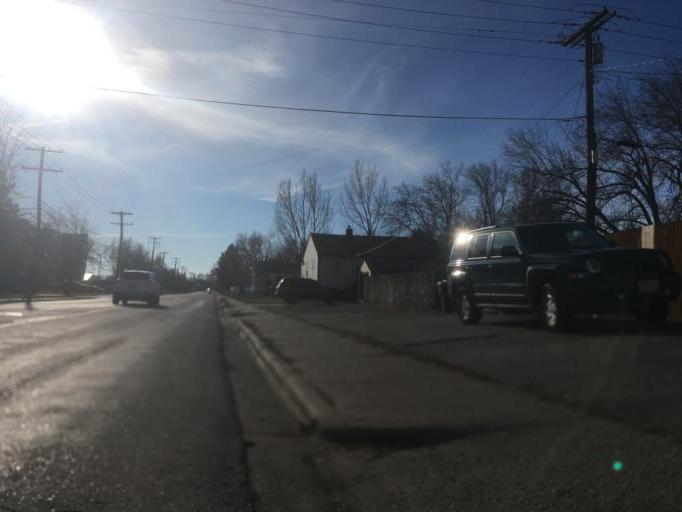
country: US
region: Montana
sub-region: Yellowstone County
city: Billings
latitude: 45.7877
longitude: -108.5591
